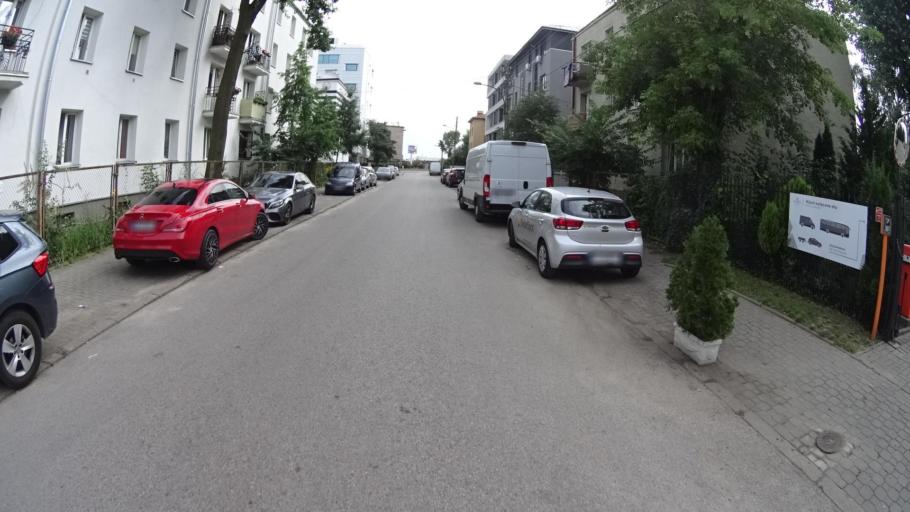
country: PL
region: Masovian Voivodeship
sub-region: Warszawa
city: Wlochy
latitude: 52.1866
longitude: 20.9569
